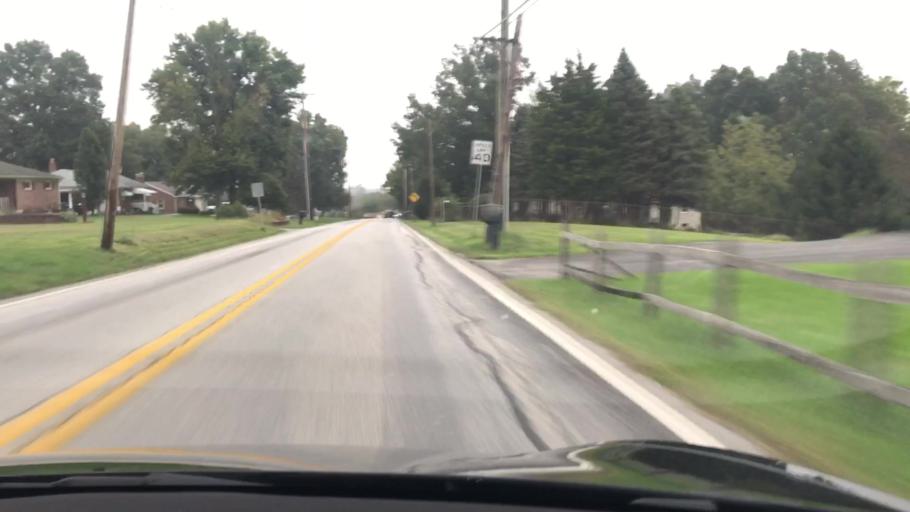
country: US
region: Pennsylvania
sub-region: York County
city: Shiloh
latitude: 40.0304
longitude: -76.7906
